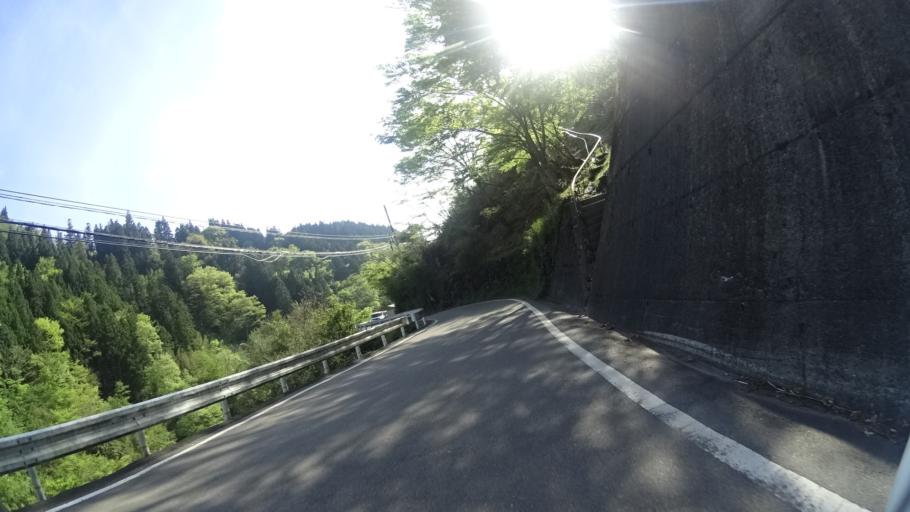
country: JP
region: Tokushima
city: Ikedacho
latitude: 33.8738
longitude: 133.9836
